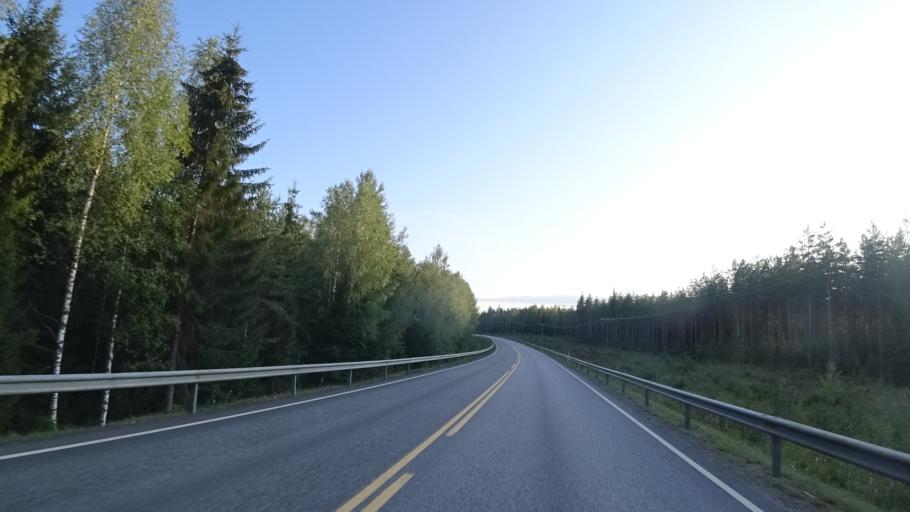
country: FI
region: South Karelia
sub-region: Lappeenranta
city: Ylaemaa
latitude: 60.8342
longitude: 28.1051
